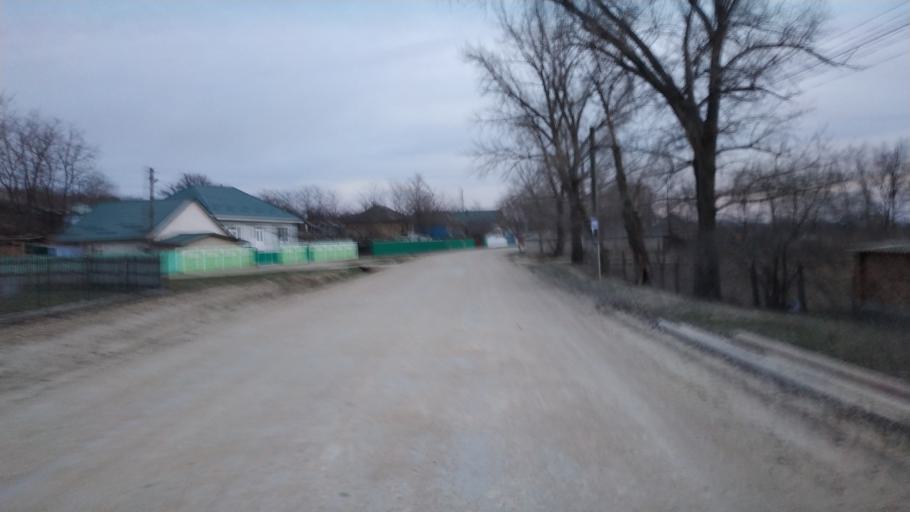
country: MD
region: Hincesti
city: Dancu
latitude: 46.7405
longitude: 28.2122
